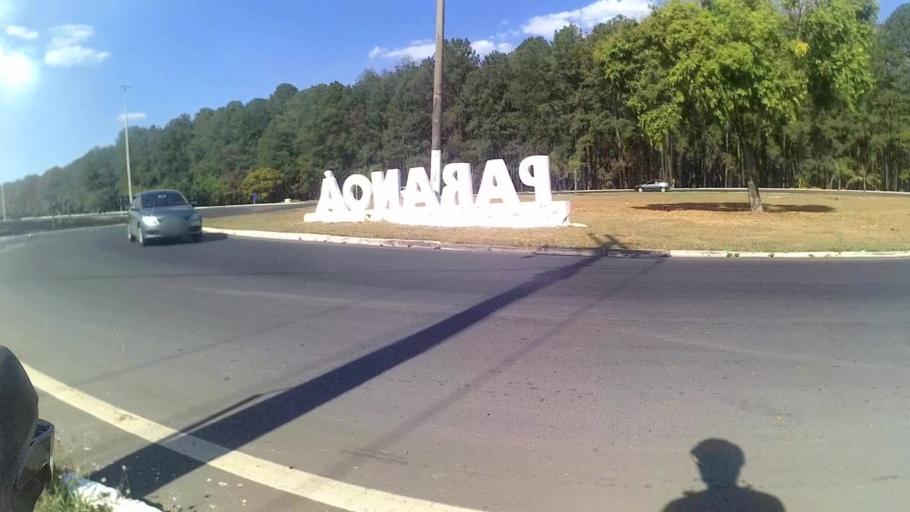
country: BR
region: Federal District
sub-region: Brasilia
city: Brasilia
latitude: -15.7828
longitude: -47.7771
